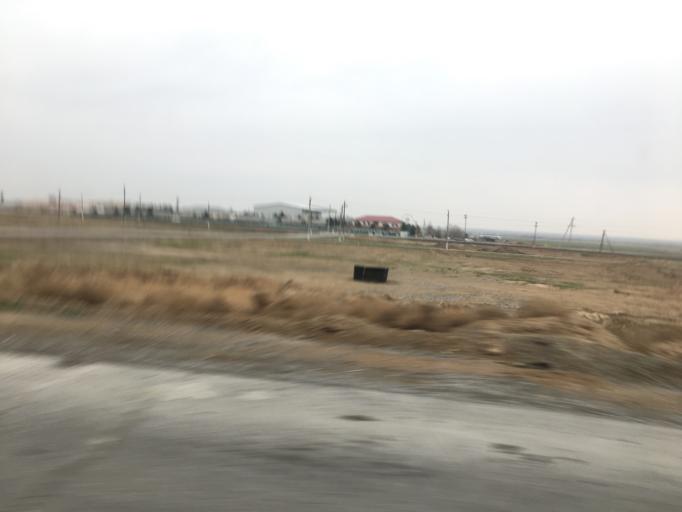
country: IR
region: Razavi Khorasan
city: Dargaz
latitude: 37.7644
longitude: 58.9094
